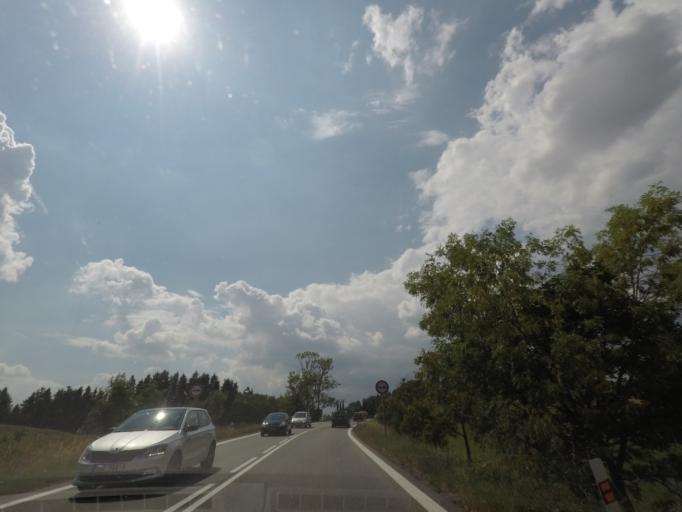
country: CZ
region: Liberecky
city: Studenec
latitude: 50.5226
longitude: 15.5695
